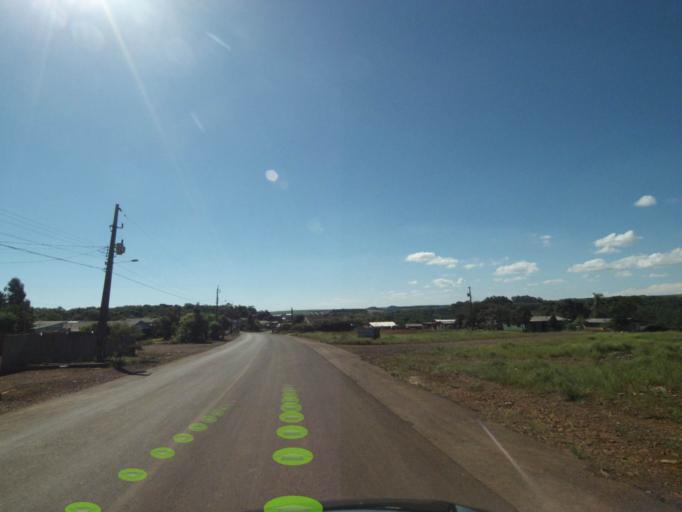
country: BR
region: Parana
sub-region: Coronel Vivida
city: Coronel Vivida
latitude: -26.1471
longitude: -52.3704
